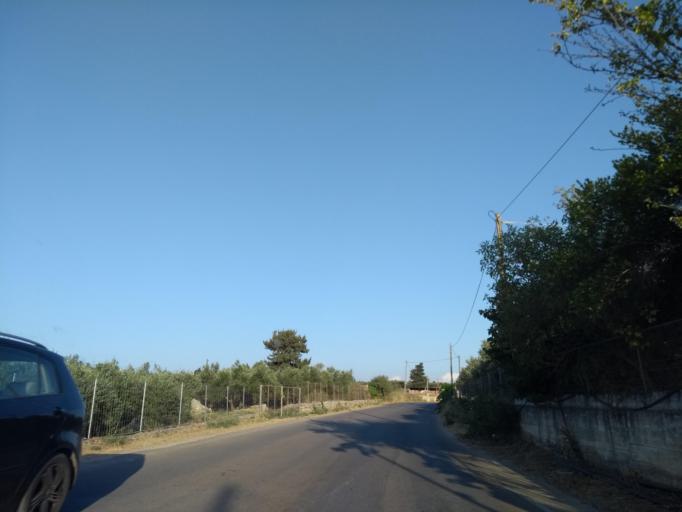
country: GR
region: Crete
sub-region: Nomos Chanias
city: Kalivai
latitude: 35.4176
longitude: 24.1909
